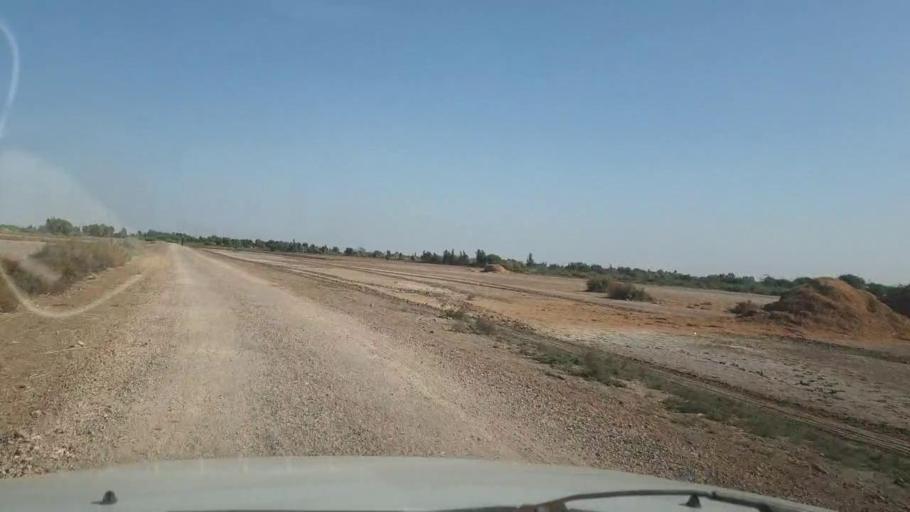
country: PK
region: Sindh
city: Mirpur Sakro
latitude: 24.4855
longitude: 67.8125
